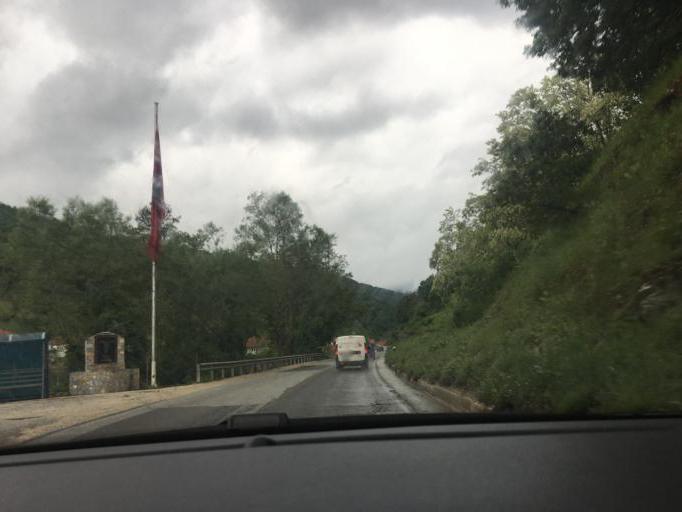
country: MK
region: Kicevo
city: Zajas
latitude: 41.6368
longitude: 20.9036
